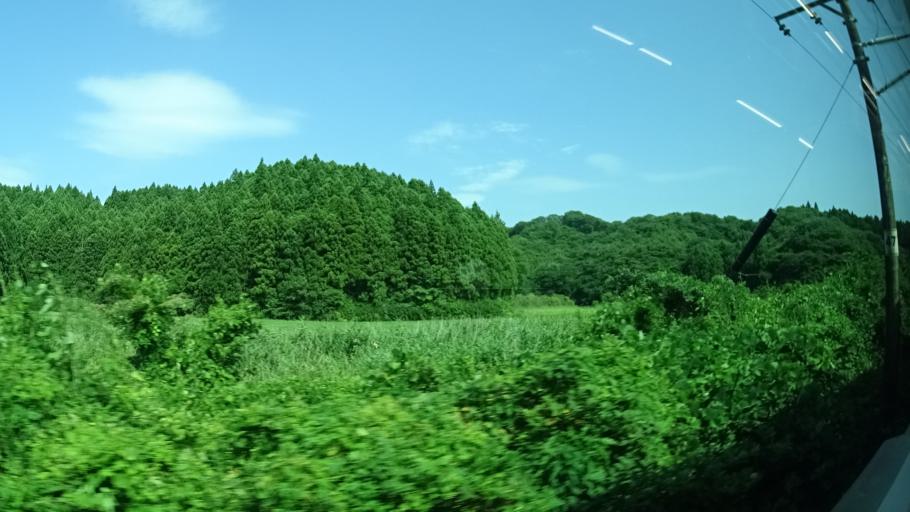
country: JP
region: Miyagi
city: Kogota
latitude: 38.4956
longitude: 141.0876
